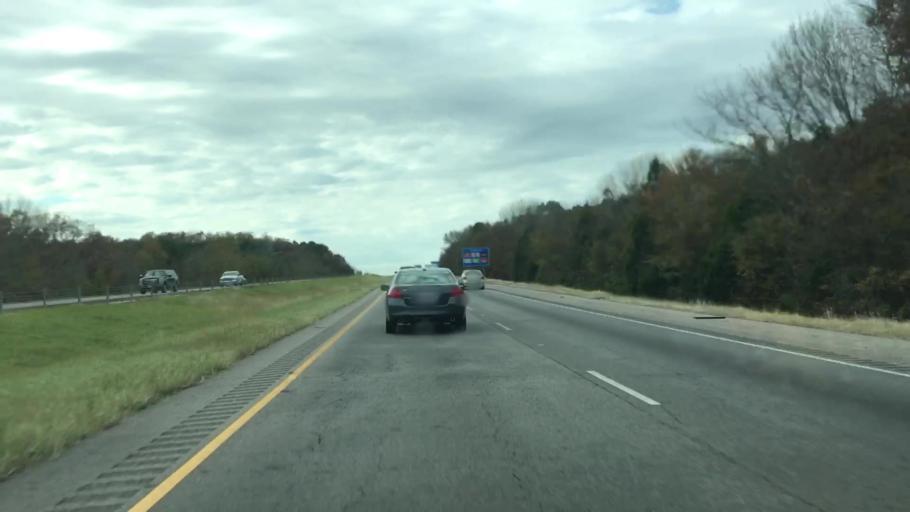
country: US
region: Arkansas
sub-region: Conway County
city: Morrilton
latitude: 35.1683
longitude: -92.6894
